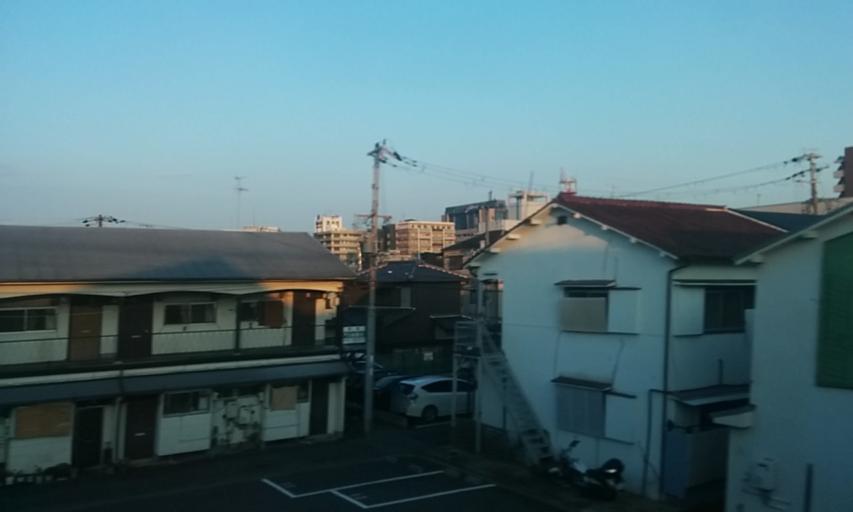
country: JP
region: Osaka
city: Ibaraki
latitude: 34.8182
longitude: 135.5648
